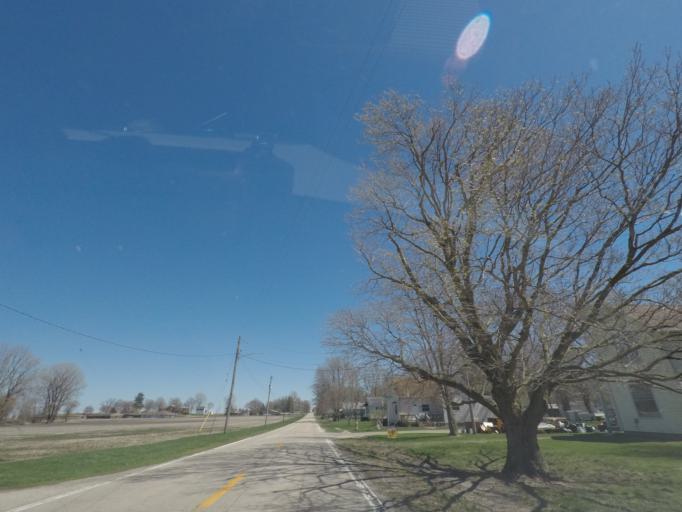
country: US
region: Illinois
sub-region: Macon County
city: Warrensburg
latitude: 39.9684
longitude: -89.1675
